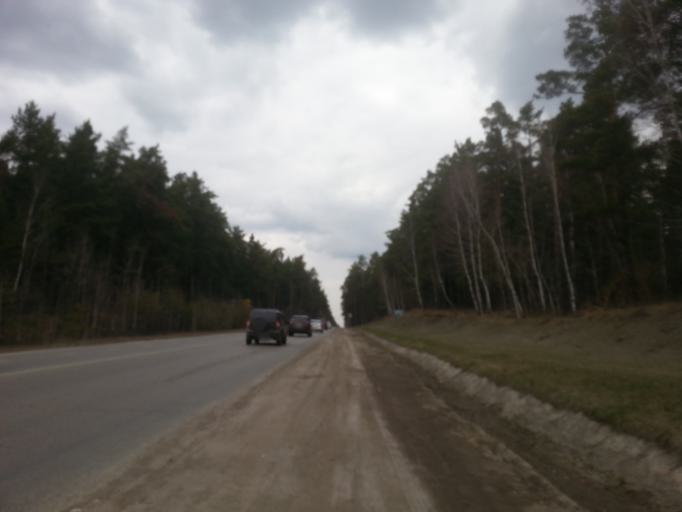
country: RU
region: Altai Krai
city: Yuzhnyy
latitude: 53.2700
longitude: 83.7251
